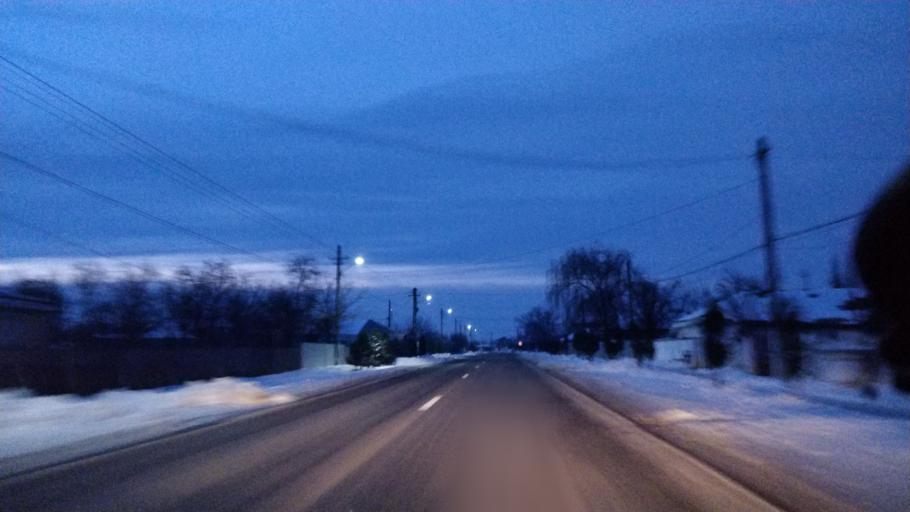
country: RO
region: Vrancea
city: Vulturu de Sus
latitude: 45.6331
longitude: 27.3843
